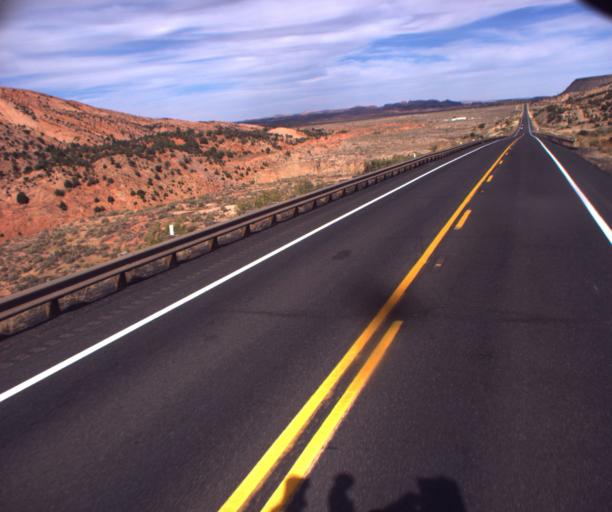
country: US
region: Arizona
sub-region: Navajo County
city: Kayenta
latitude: 36.6625
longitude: -110.4172
